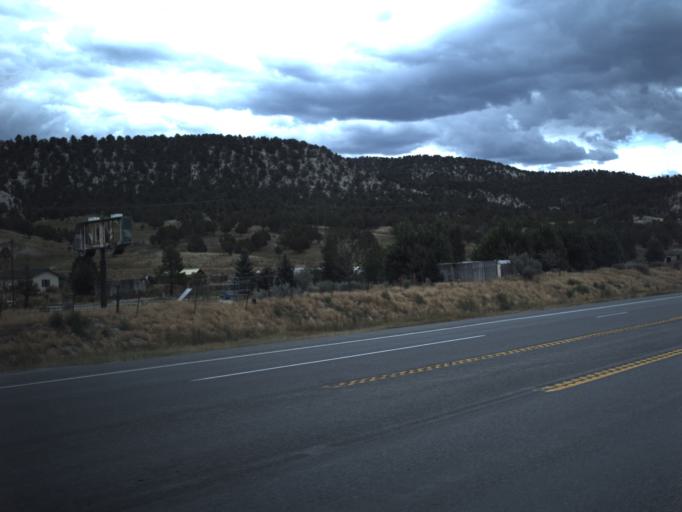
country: US
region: Utah
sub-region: Utah County
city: Mapleton
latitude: 39.9735
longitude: -111.3380
